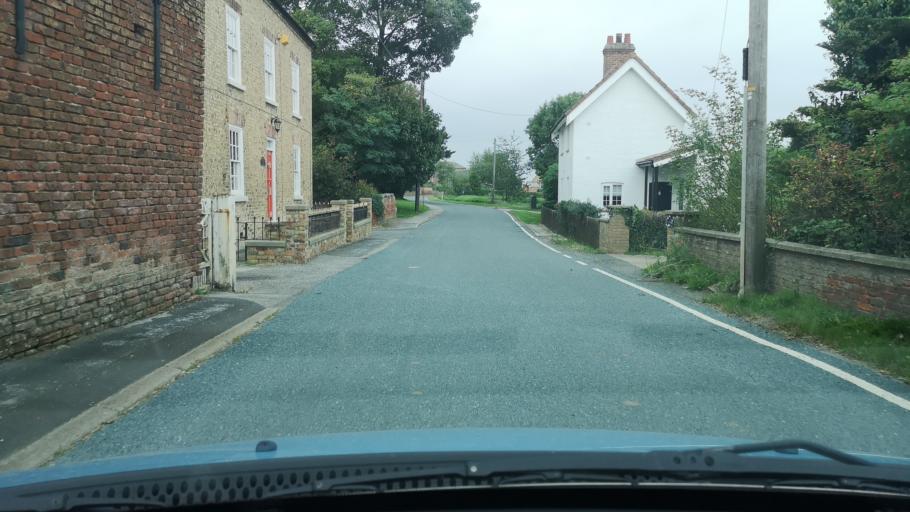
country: GB
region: England
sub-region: North Lincolnshire
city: Burton upon Stather
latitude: 53.6766
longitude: -0.7235
